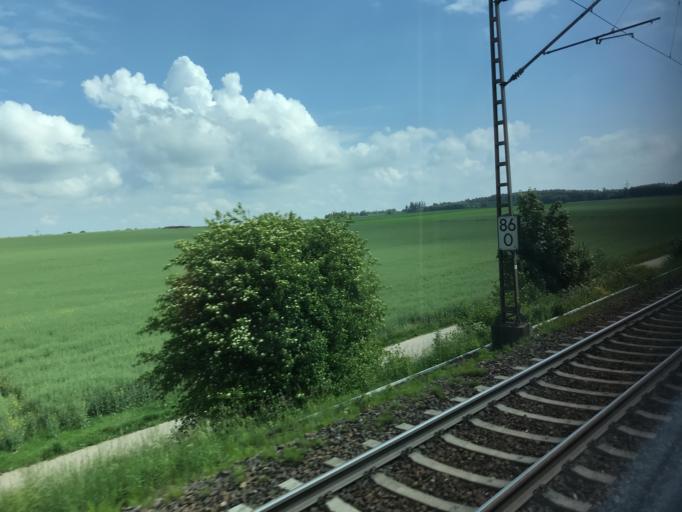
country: DE
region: Baden-Wuerttemberg
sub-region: Tuebingen Region
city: Beimerstetten
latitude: 48.4510
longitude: 9.9886
